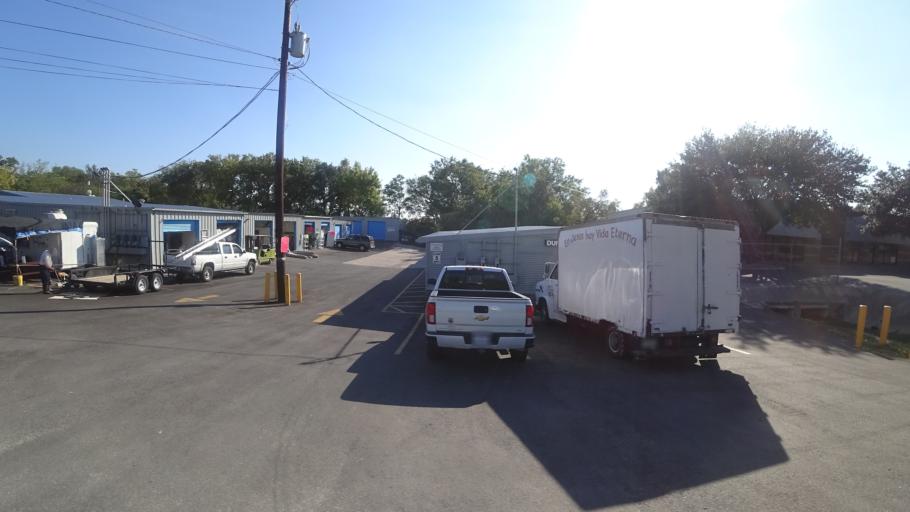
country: US
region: Texas
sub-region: Travis County
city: Wells Branch
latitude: 30.3514
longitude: -97.6732
